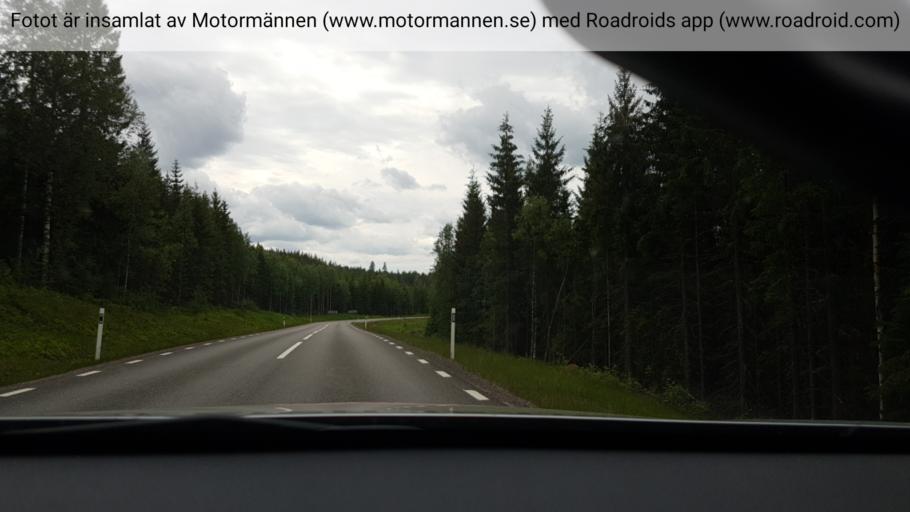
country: SE
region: Vaermland
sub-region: Torsby Kommun
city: Torsby
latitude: 60.3506
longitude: 13.1688
